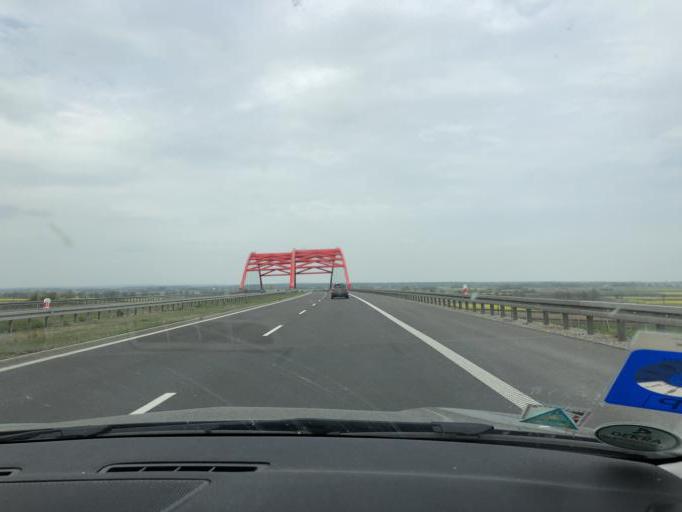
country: PL
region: Subcarpathian Voivodeship
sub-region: Powiat przeworski
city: Rozborz
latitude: 50.0613
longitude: 22.5666
